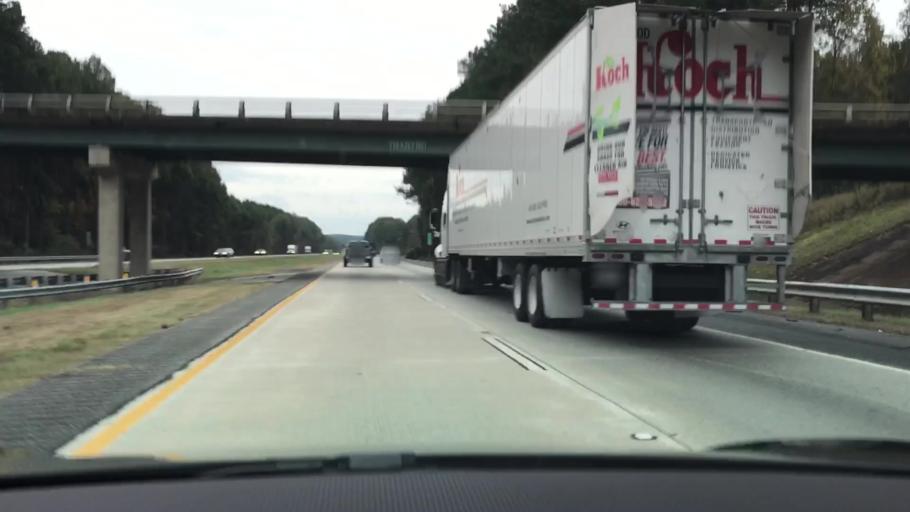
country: US
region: Georgia
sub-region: Greene County
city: Greensboro
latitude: 33.5477
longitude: -83.1689
